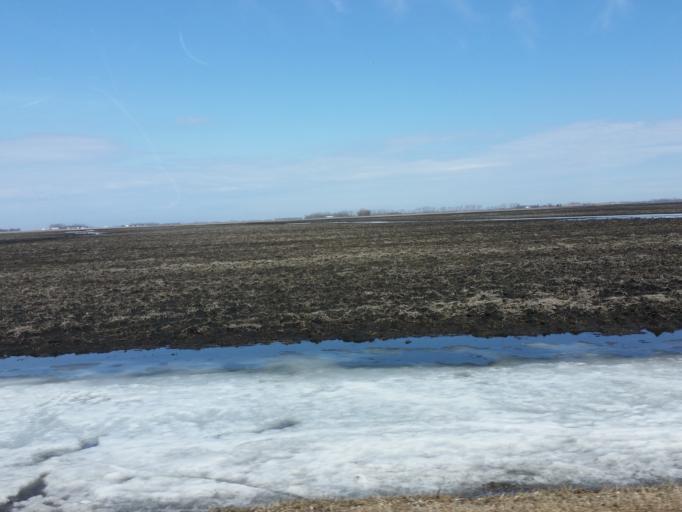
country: US
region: North Dakota
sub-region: Walsh County
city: Grafton
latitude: 48.3243
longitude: -97.2038
